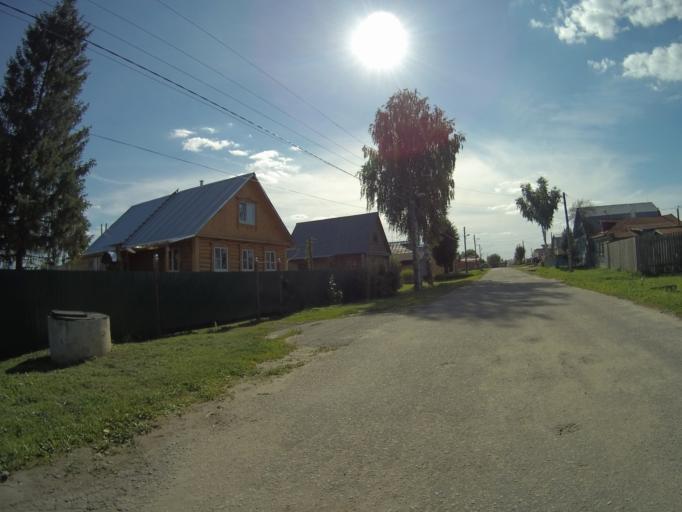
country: RU
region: Vladimir
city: Vorsha
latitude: 56.0954
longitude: 40.1926
